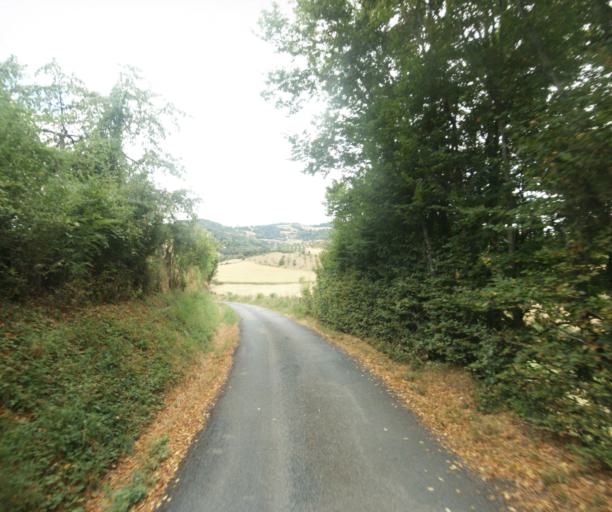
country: FR
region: Rhone-Alpes
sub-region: Departement du Rhone
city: Bessenay
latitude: 45.7891
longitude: 4.5176
